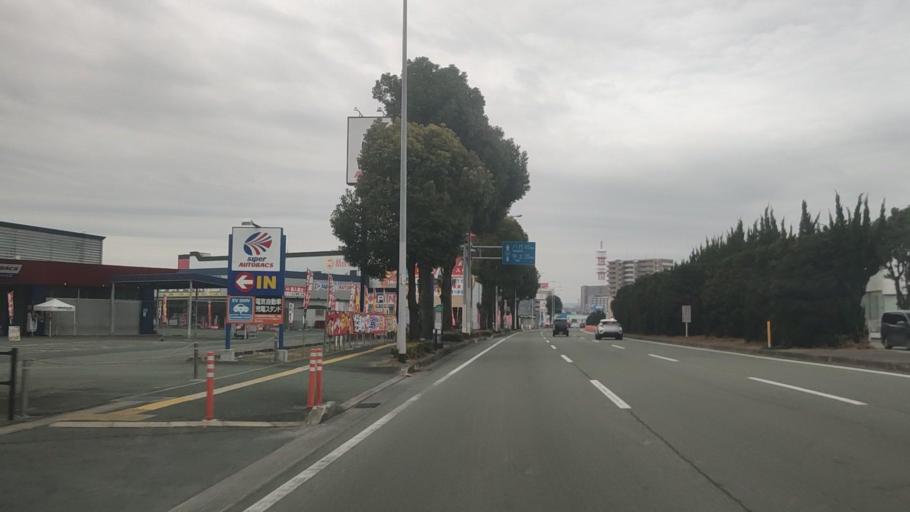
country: JP
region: Kumamoto
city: Kumamoto
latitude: 32.8159
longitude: 130.7491
